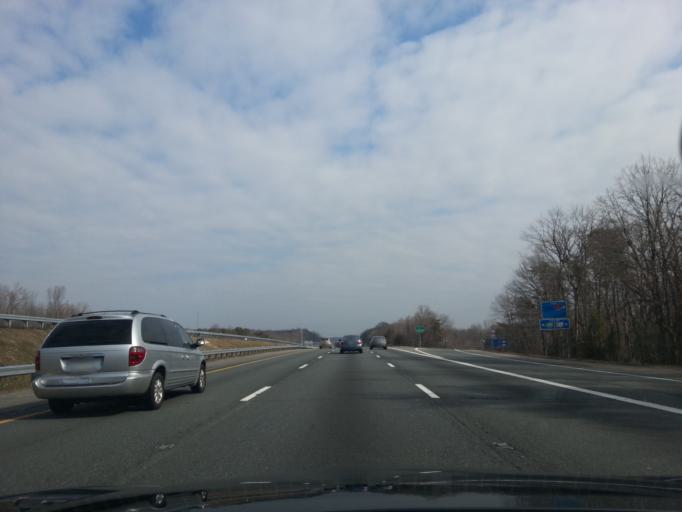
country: US
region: Virginia
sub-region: Prince William County
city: Triangle
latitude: 38.5465
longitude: -77.3443
